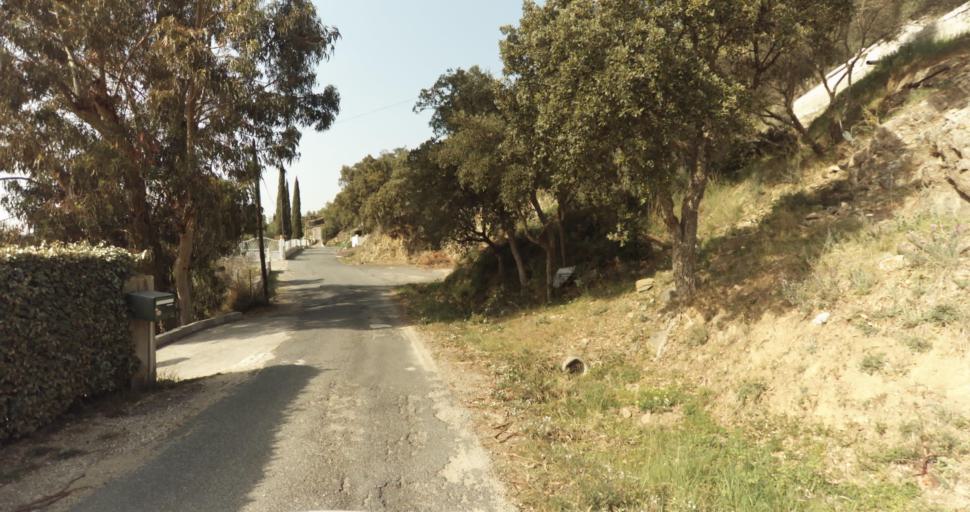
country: FR
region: Provence-Alpes-Cote d'Azur
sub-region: Departement du Var
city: Bormes-les-Mimosas
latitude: 43.1474
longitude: 6.3289
